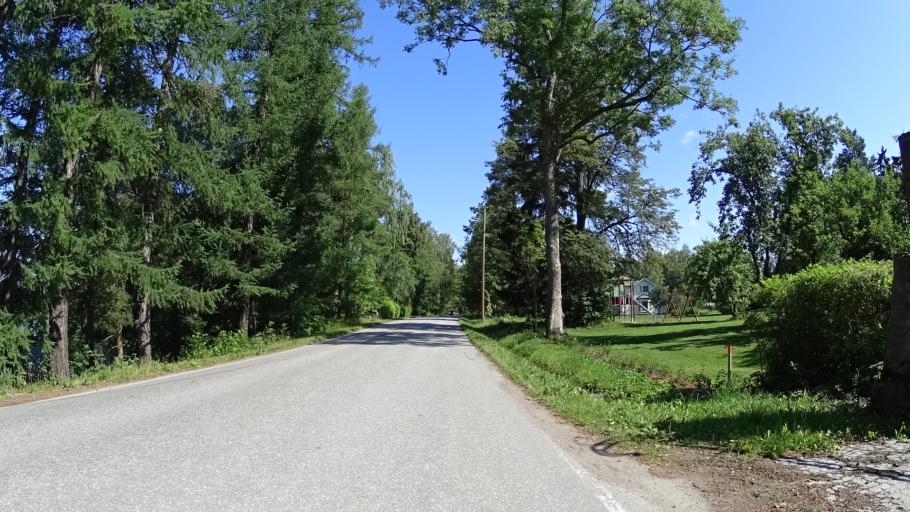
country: FI
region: Uusimaa
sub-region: Helsinki
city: Tuusula
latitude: 60.4267
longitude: 25.0483
